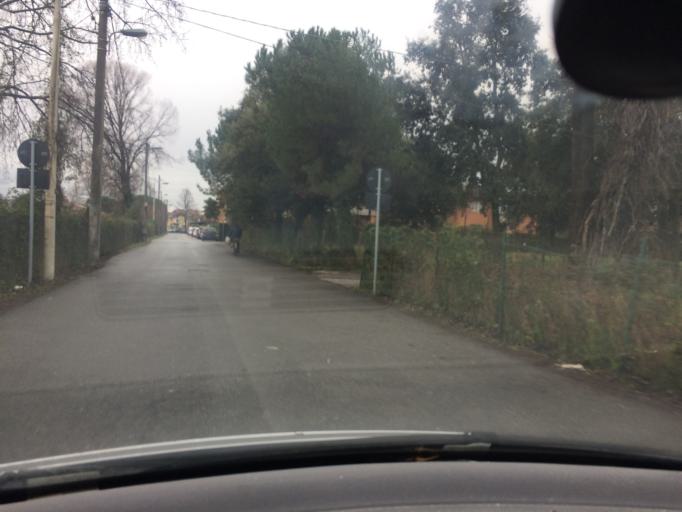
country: IT
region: Tuscany
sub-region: Provincia di Massa-Carrara
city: Massa
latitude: 44.0173
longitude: 10.0922
